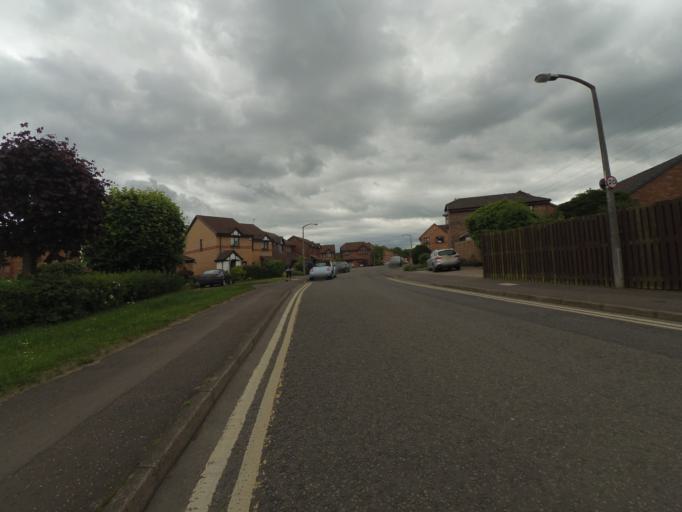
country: GB
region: Scotland
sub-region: East Lothian
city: Musselburgh
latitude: 55.9406
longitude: -3.0986
